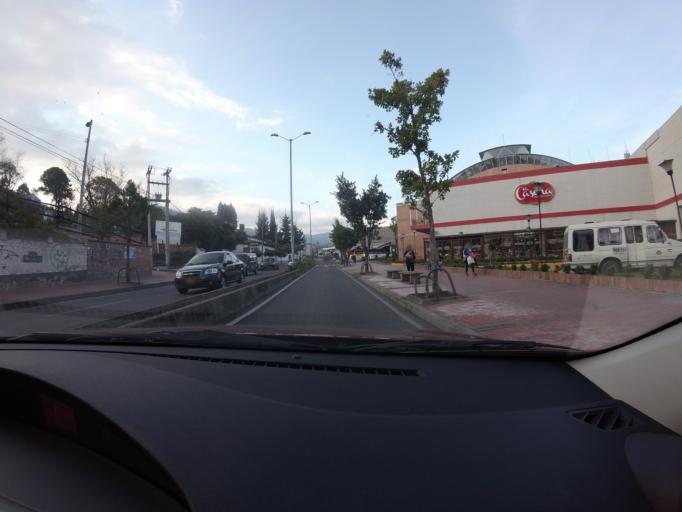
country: CO
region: Cundinamarca
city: Zipaquira
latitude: 5.0181
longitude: -74.0048
